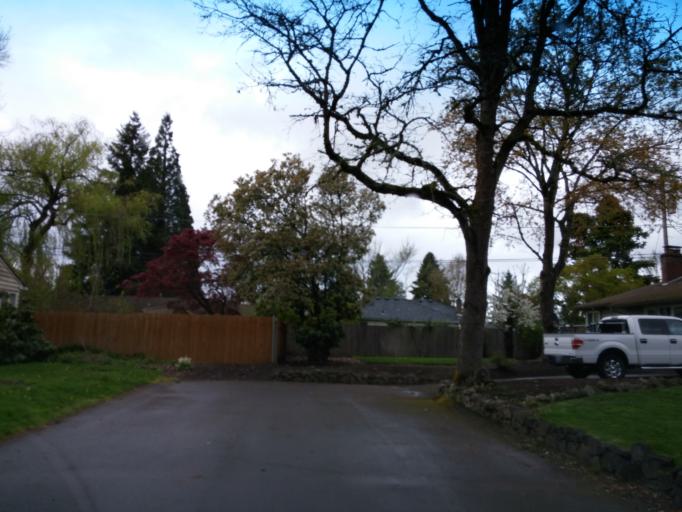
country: US
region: Oregon
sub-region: Washington County
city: Cedar Mill
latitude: 45.5193
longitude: -122.8179
